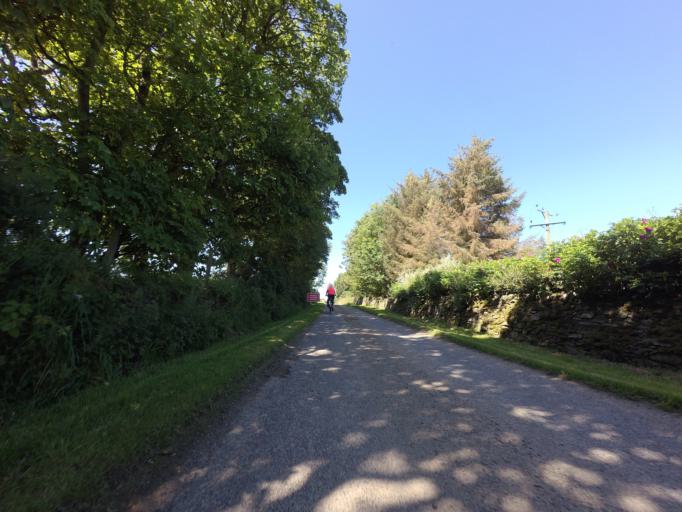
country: GB
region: Scotland
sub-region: Aberdeenshire
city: Macduff
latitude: 57.6381
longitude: -2.4944
